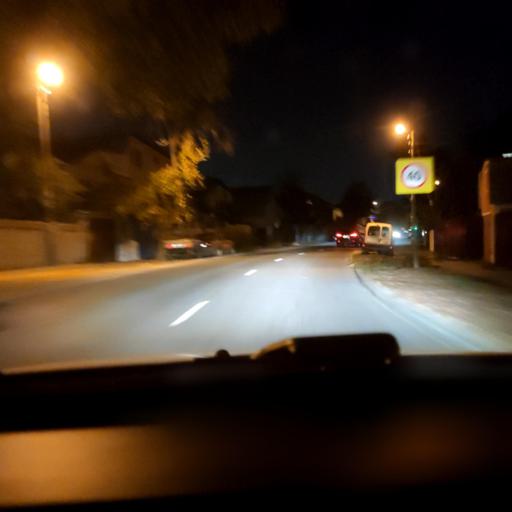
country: RU
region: Voronezj
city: Voronezh
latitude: 51.6316
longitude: 39.1897
